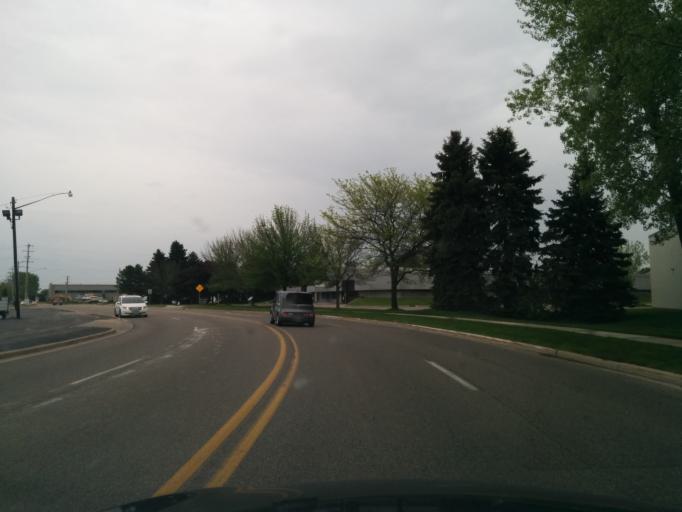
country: US
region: Michigan
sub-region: Ottawa County
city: Grand Haven
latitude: 43.0667
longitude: -86.2151
